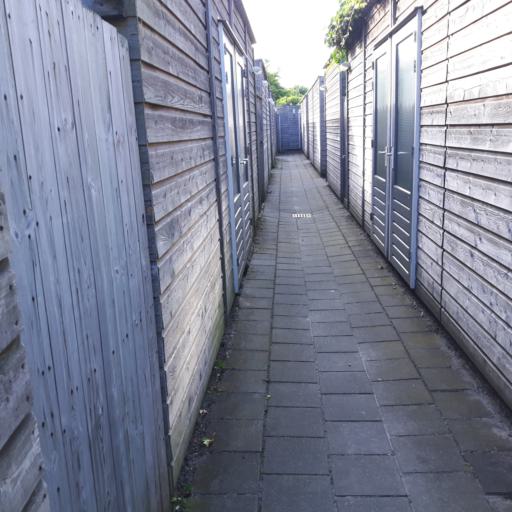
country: NL
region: Utrecht
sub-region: Gemeente Woerden
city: Woerden
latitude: 52.0799
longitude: 4.9080
